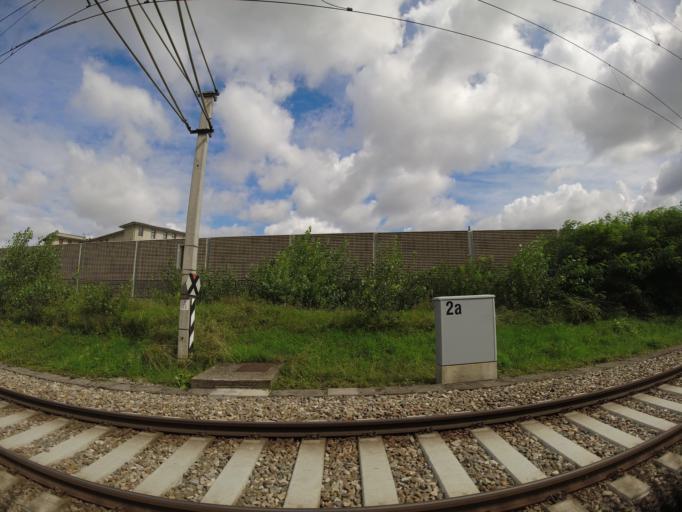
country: AT
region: Lower Austria
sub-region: Politischer Bezirk Modling
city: Vosendorf
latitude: 48.1642
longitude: 16.3304
